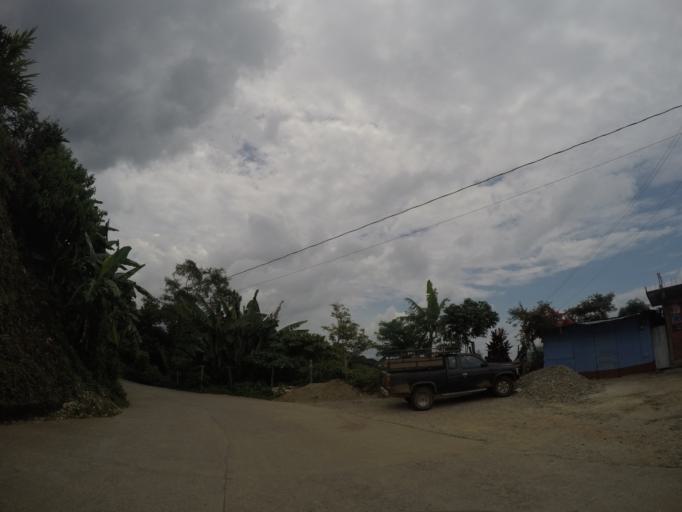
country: MX
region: Oaxaca
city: Pluma Hidalgo
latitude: 15.9209
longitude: -96.4172
